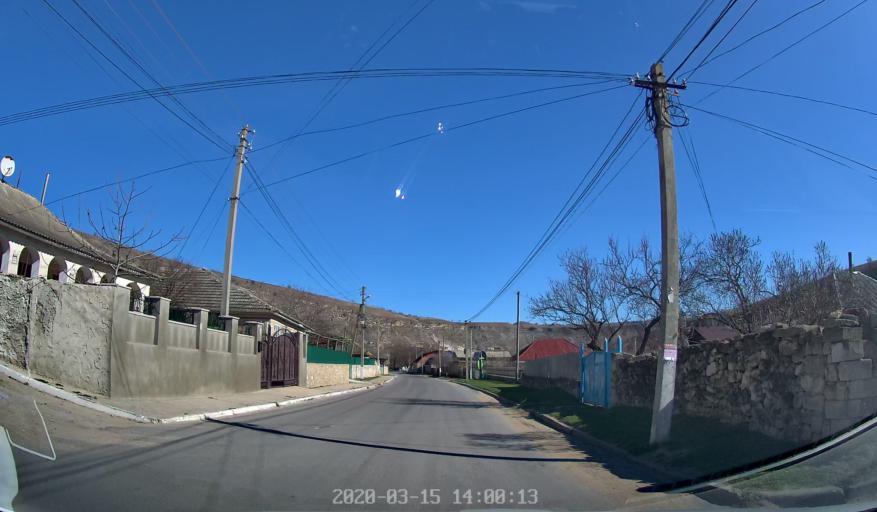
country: MD
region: Telenesti
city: Cocieri
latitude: 47.3107
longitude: 28.9804
